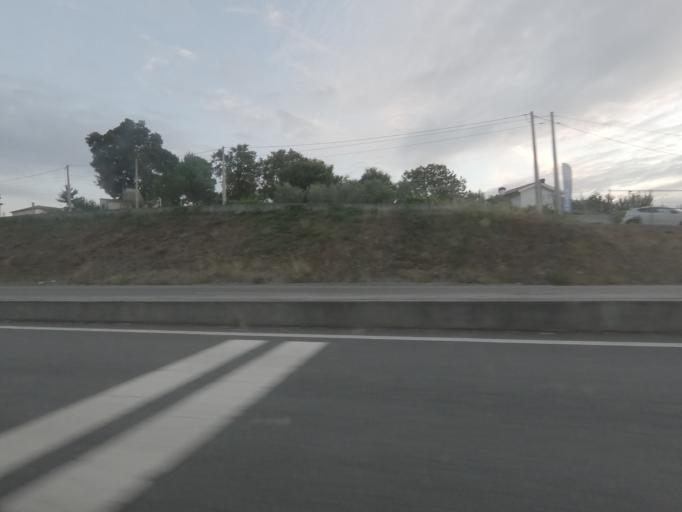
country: PT
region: Vila Real
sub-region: Vila Real
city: Vila Real
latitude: 41.2859
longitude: -7.7325
